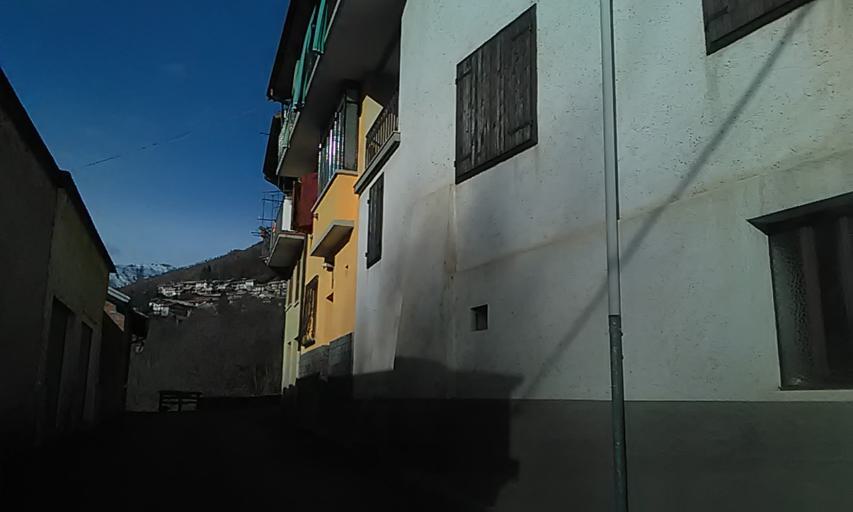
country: IT
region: Piedmont
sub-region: Provincia di Biella
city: Coggiola
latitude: 45.6962
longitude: 8.1797
